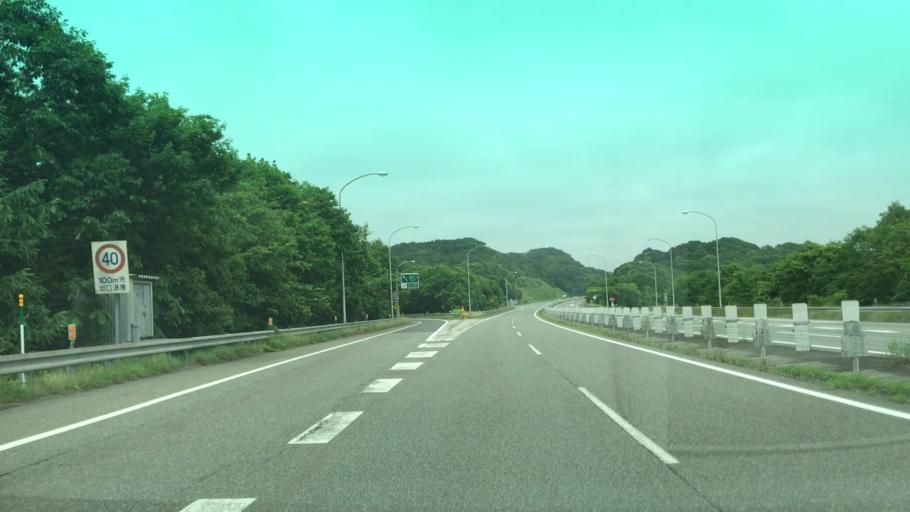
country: JP
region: Hokkaido
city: Tomakomai
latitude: 42.6311
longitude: 141.4874
